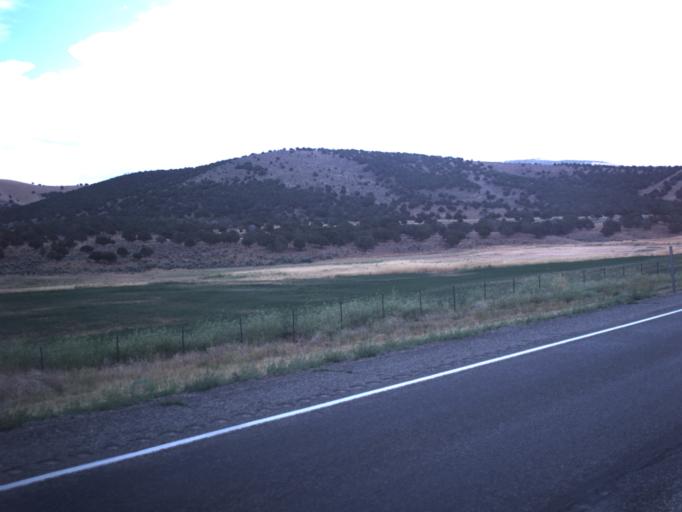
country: US
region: Utah
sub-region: Sanpete County
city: Fountain Green
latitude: 39.6432
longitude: -111.6375
